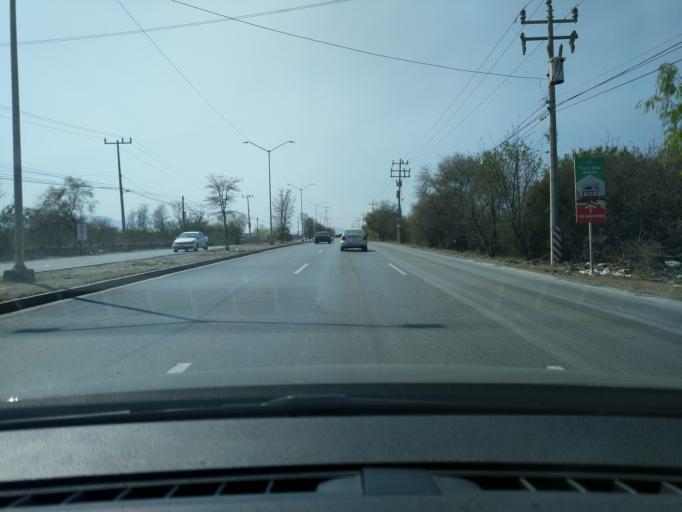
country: MX
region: Nuevo Leon
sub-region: Garcia
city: Valle de Lincoln
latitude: 25.7906
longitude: -100.5020
